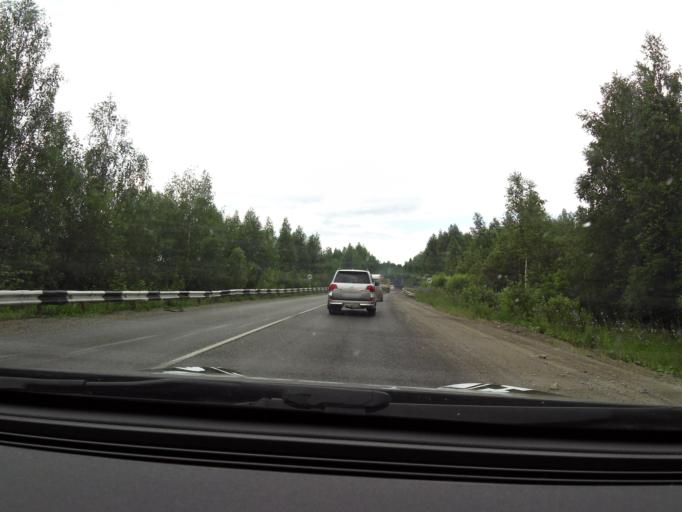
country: RU
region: Chelyabinsk
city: Sim
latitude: 54.9990
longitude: 57.6255
